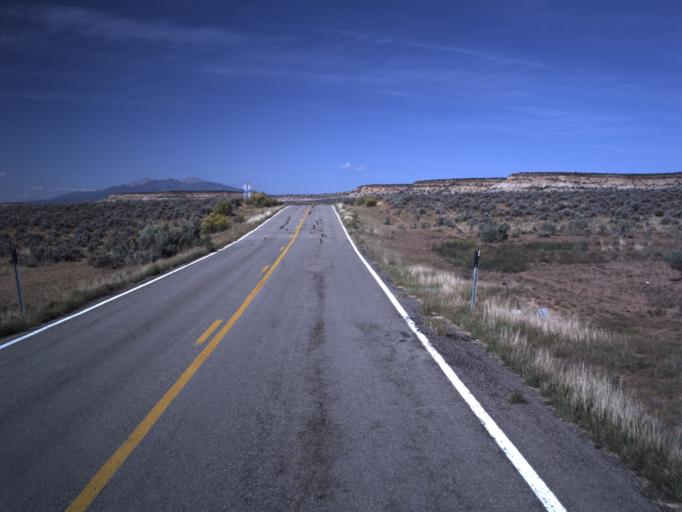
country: US
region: Utah
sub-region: San Juan County
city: Monticello
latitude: 38.0148
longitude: -109.4322
